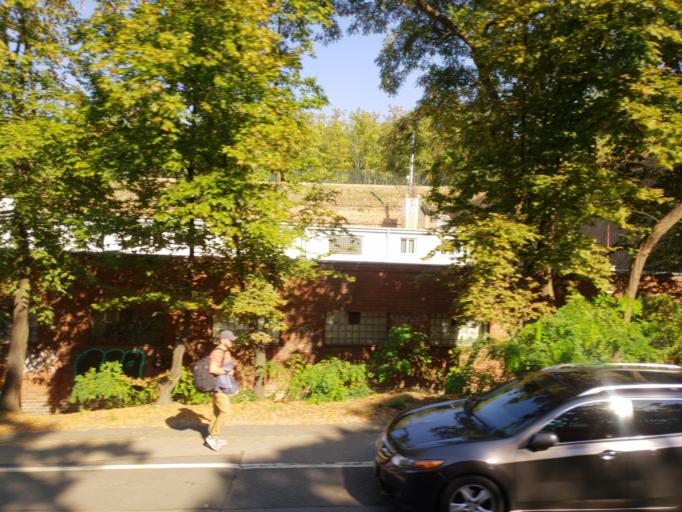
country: CZ
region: Praha
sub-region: Praha 1
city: Mala Strana
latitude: 50.0839
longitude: 14.3876
